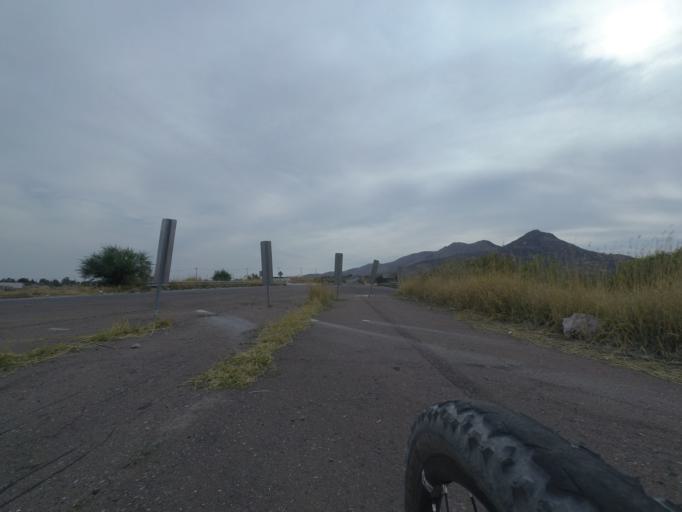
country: MX
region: Aguascalientes
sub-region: Aguascalientes
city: La Loma de los Negritos
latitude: 21.8917
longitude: -102.3980
